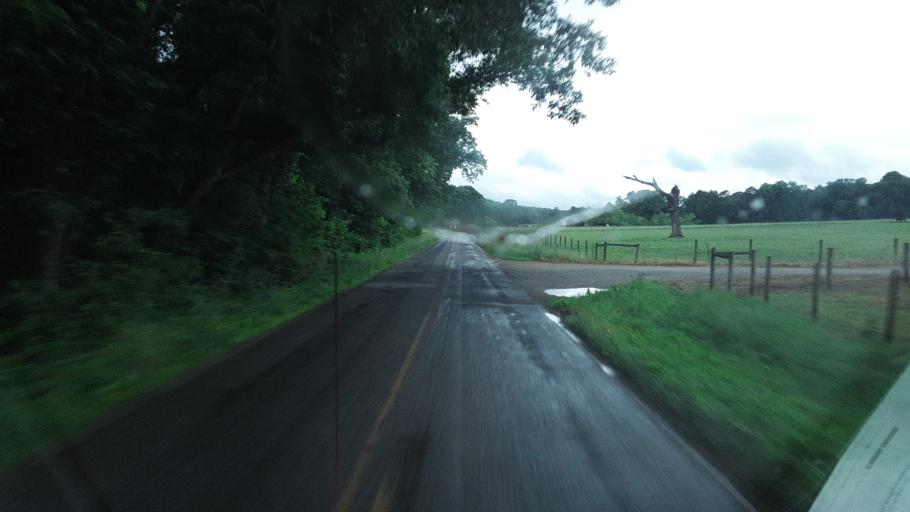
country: US
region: North Carolina
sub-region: Yadkin County
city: Jonesville
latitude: 36.1072
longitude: -80.8850
